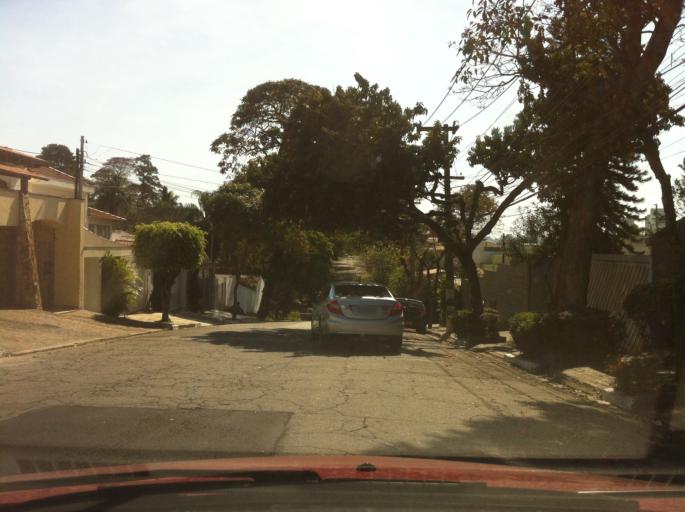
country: BR
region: Sao Paulo
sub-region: Sao Paulo
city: Sao Paulo
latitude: -23.6087
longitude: -46.6498
